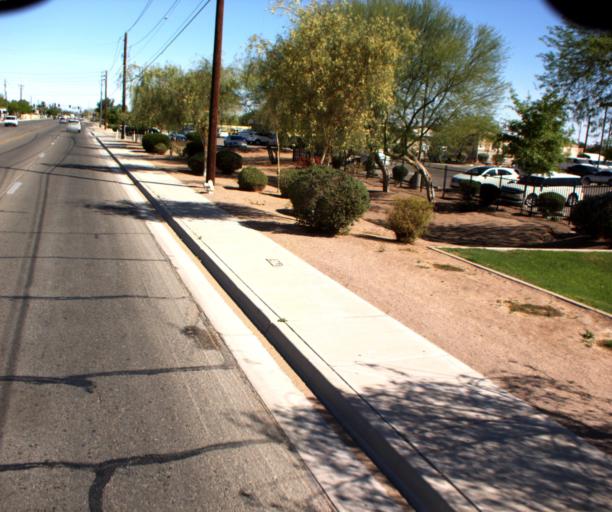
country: US
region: Arizona
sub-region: Yuma County
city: Yuma
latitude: 32.6779
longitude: -114.6502
